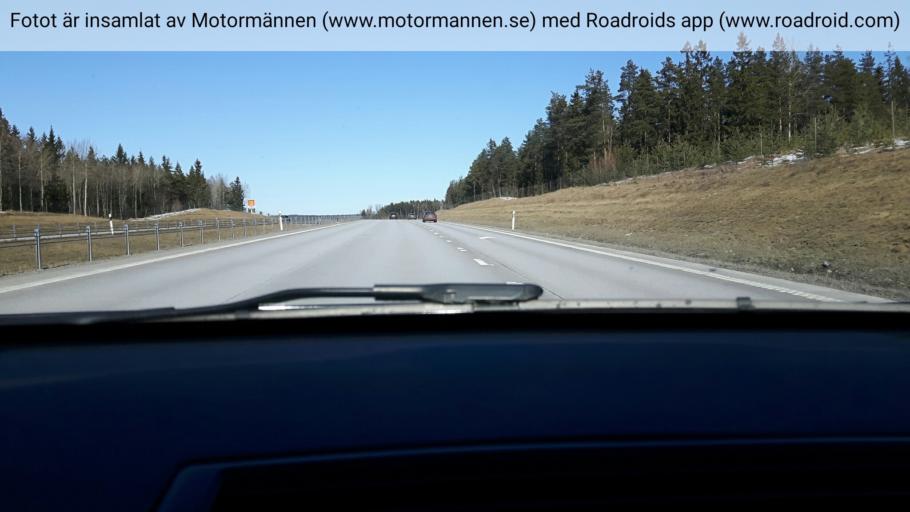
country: SE
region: Uppsala
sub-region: Uppsala Kommun
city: Gamla Uppsala
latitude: 59.9348
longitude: 17.6610
